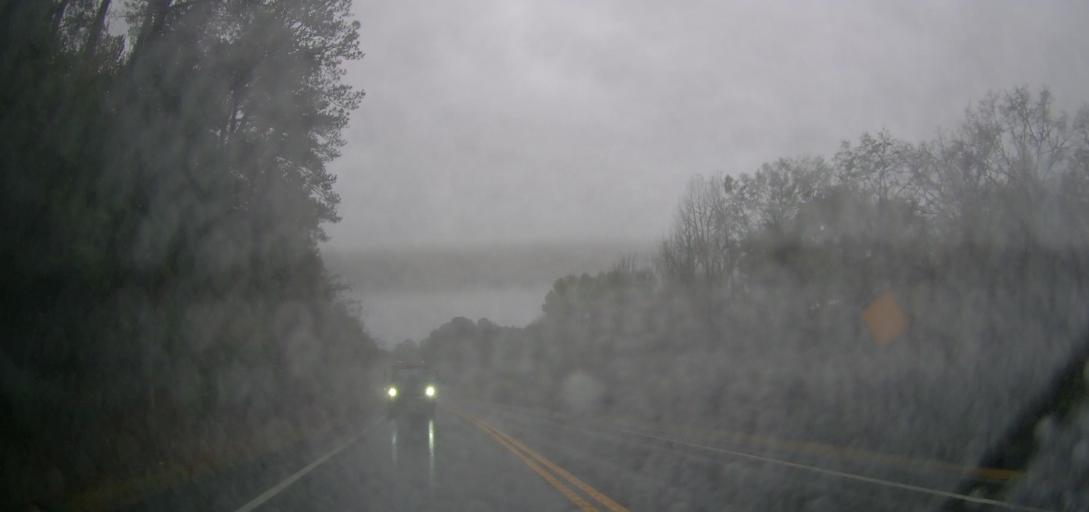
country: US
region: Georgia
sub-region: Putnam County
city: Eatonton
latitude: 33.1875
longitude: -83.4360
